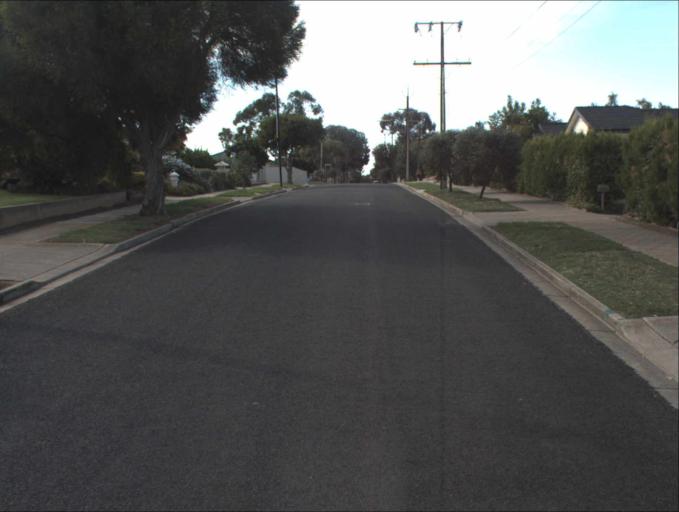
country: AU
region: South Australia
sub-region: Port Adelaide Enfield
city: Klemzig
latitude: -34.8720
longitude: 138.6471
